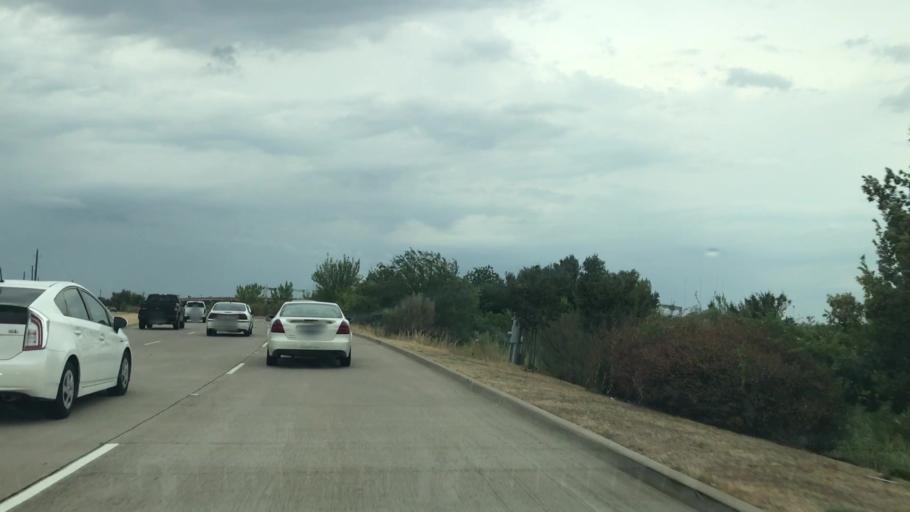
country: US
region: Texas
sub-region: Dallas County
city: Carrollton
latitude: 32.9603
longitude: -96.9239
